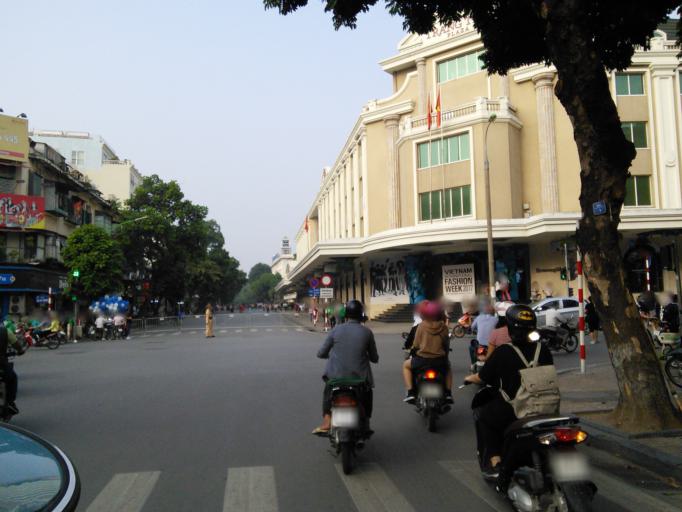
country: VN
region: Ha Noi
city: Hoan Kiem
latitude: 21.0240
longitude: 105.8530
